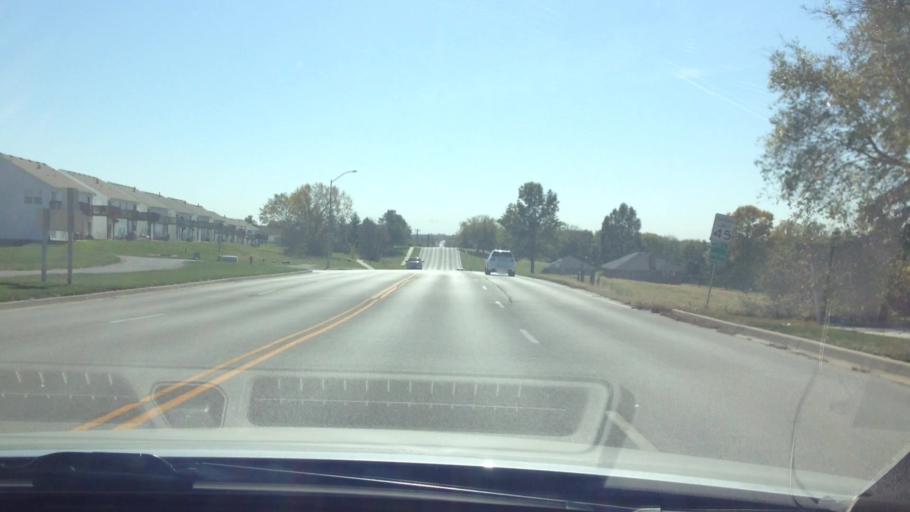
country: US
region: Missouri
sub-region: Platte County
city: Platte City
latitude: 39.3469
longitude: -94.7610
